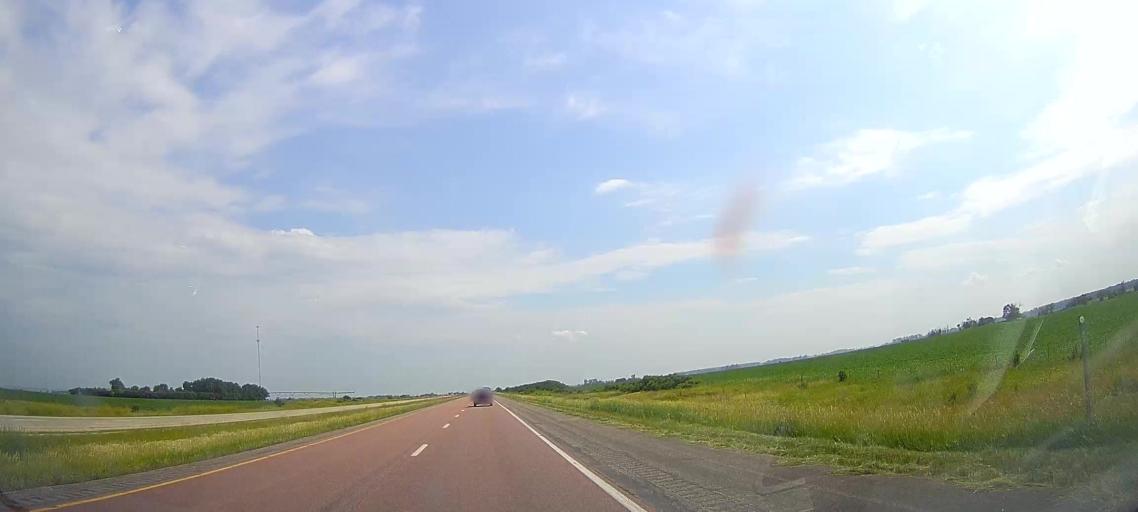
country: US
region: Iowa
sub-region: Monona County
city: Onawa
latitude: 41.9615
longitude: -96.1028
